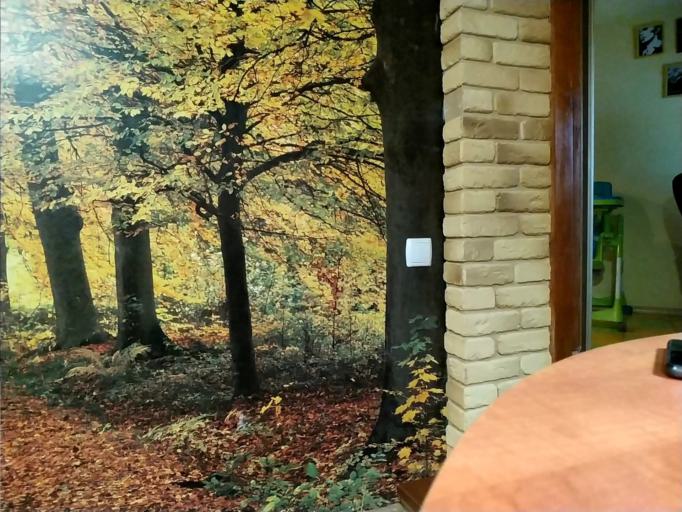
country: BY
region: Minsk
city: Il'ya
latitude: 54.4242
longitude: 27.5207
